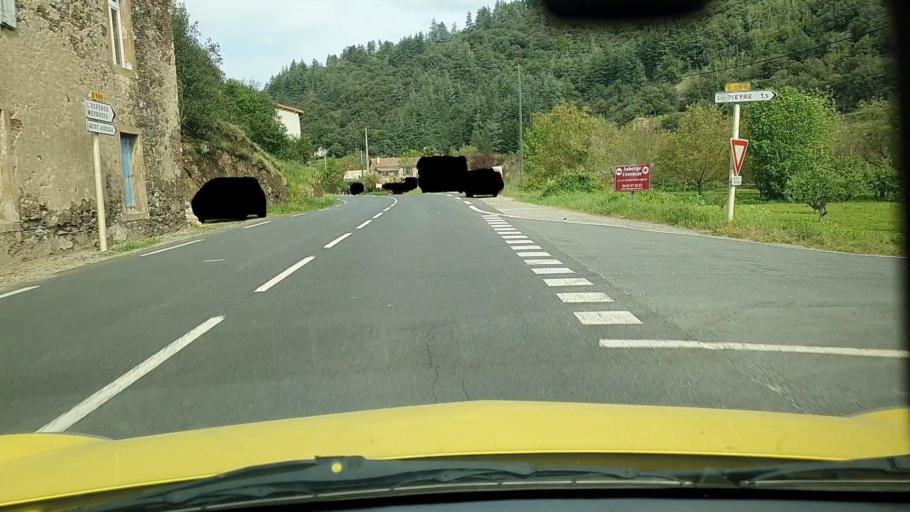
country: FR
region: Languedoc-Roussillon
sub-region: Departement du Gard
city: Valleraugue
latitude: 44.0784
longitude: 3.6527
